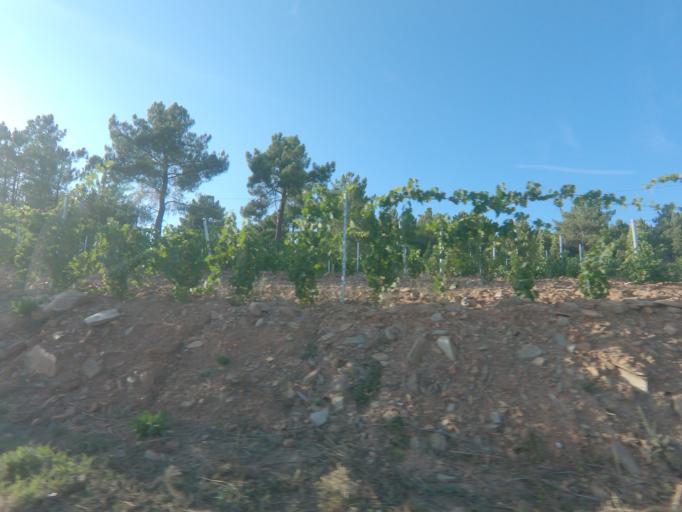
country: PT
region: Vila Real
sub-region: Sabrosa
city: Sabrosa
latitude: 41.2722
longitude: -7.5219
